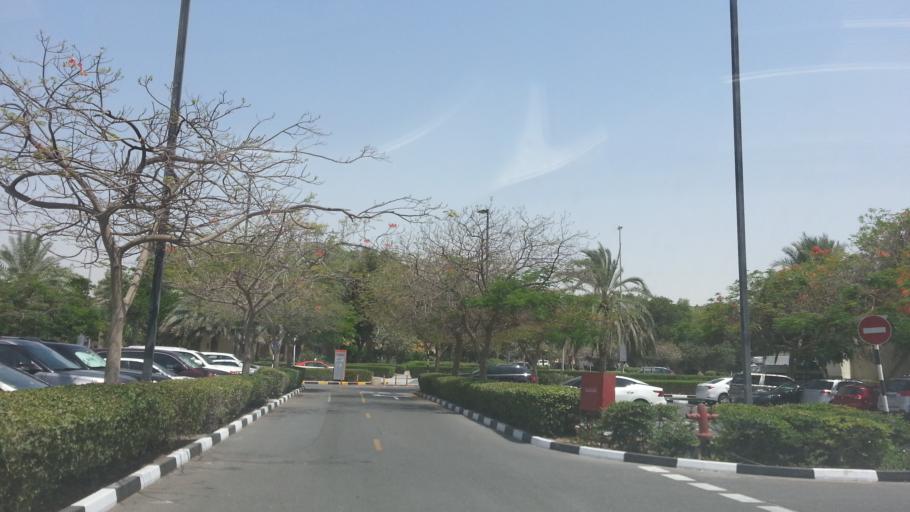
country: AE
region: Dubai
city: Dubai
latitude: 25.0448
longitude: 55.1215
